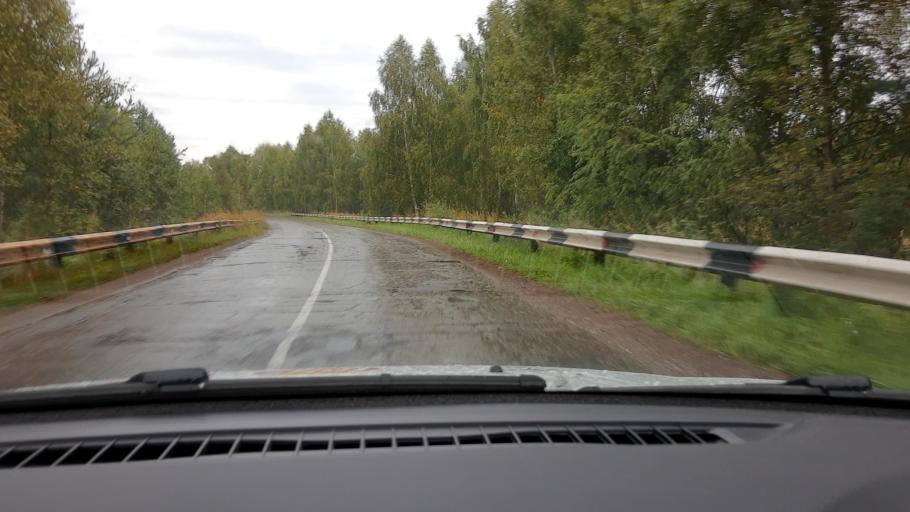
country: RU
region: Nizjnij Novgorod
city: Bogorodsk
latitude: 56.1046
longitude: 43.4197
